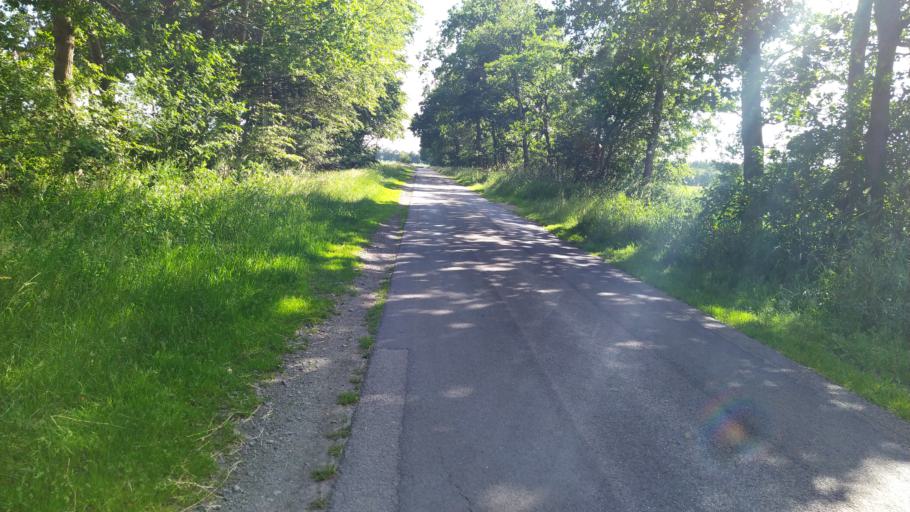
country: DE
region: Lower Saxony
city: Lintig
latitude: 53.6419
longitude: 8.9046
